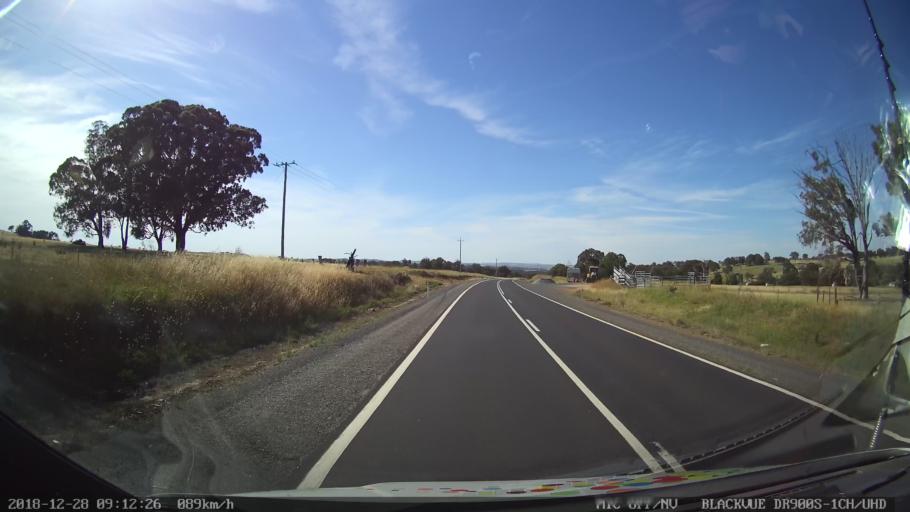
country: AU
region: New South Wales
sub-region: Upper Lachlan Shire
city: Crookwell
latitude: -34.2554
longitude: 149.3415
